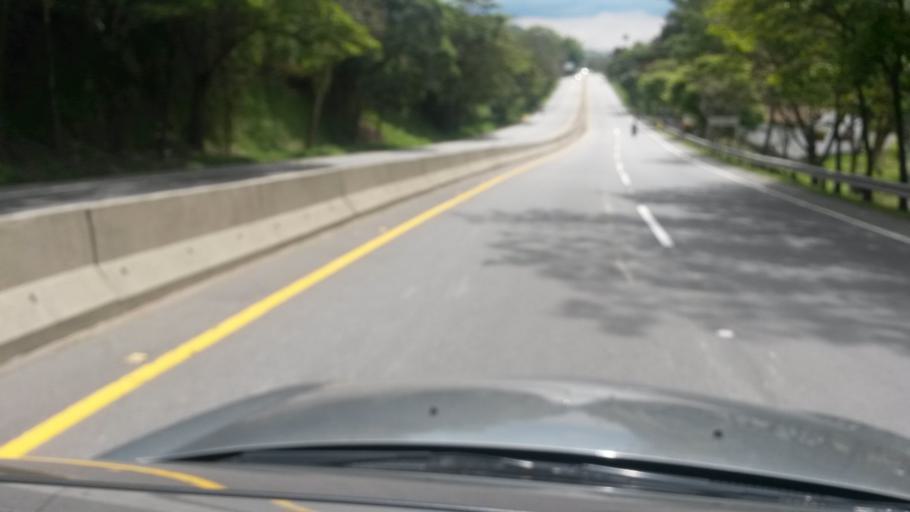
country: CO
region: Caldas
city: Palestina
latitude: 5.0115
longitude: -75.5942
